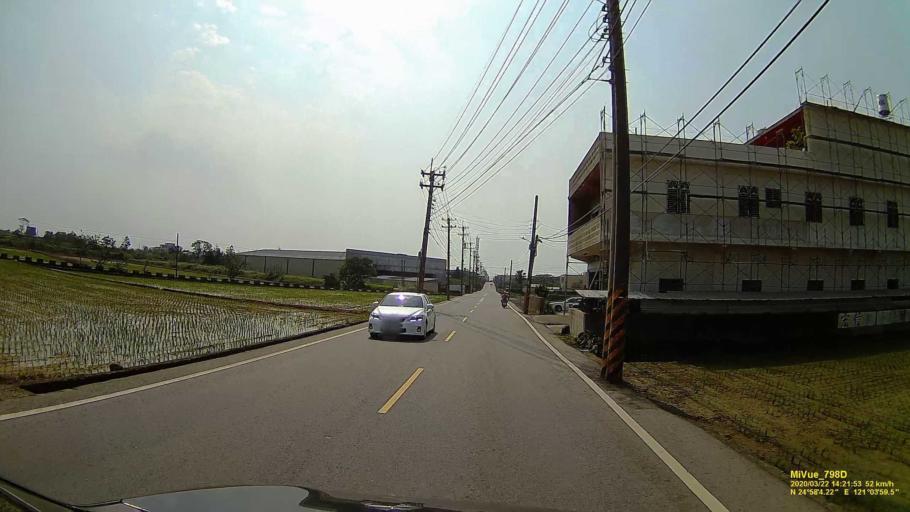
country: TW
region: Taiwan
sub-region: Hsinchu
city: Zhubei
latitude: 24.9678
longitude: 121.0663
